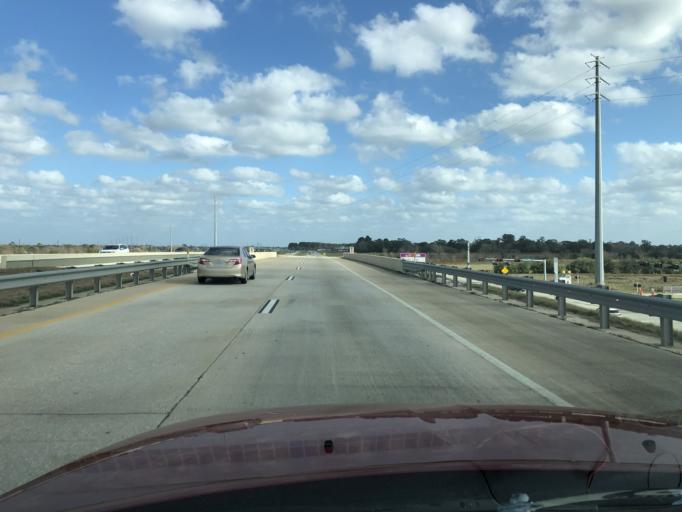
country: US
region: Texas
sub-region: Harris County
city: Cypress
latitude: 30.0533
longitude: -95.7349
